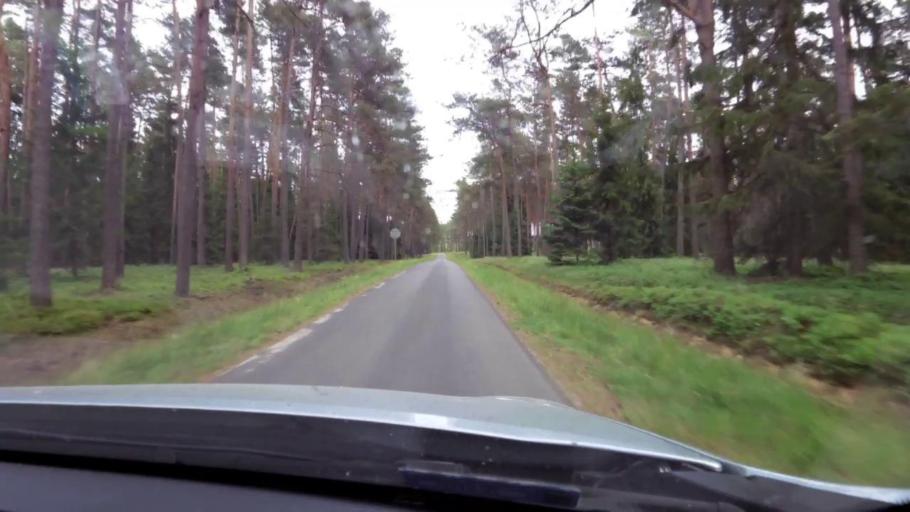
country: PL
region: Pomeranian Voivodeship
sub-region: Powiat bytowski
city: Trzebielino
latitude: 54.1960
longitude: 17.0098
